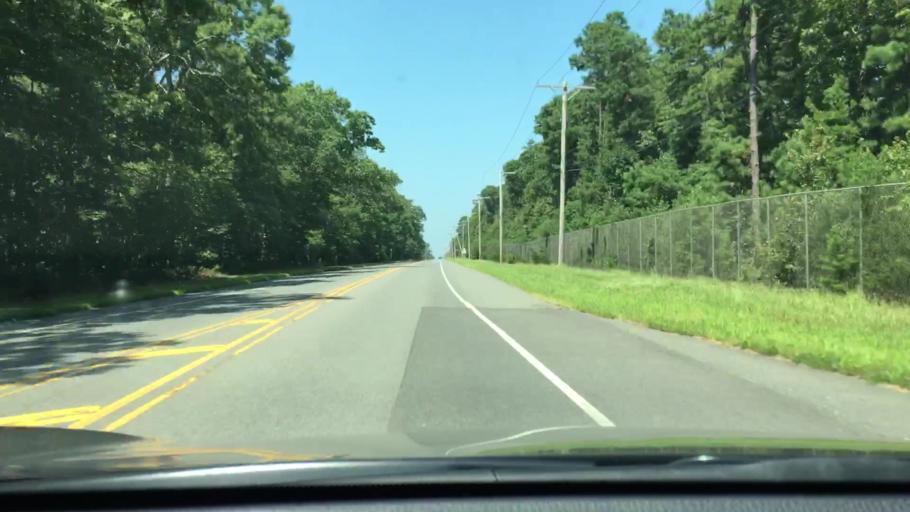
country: US
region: New Jersey
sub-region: Cumberland County
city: Laurel Lake
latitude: 39.3561
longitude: -75.0657
